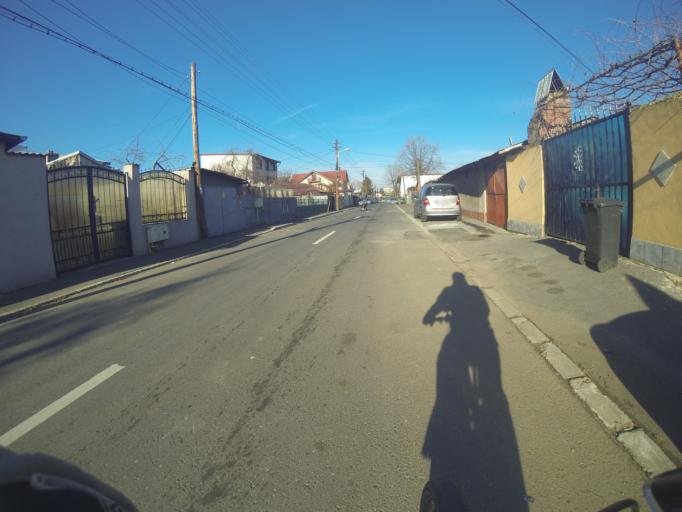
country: RO
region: Bucuresti
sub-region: Municipiul Bucuresti
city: Bucuresti
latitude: 44.3988
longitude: 26.0697
